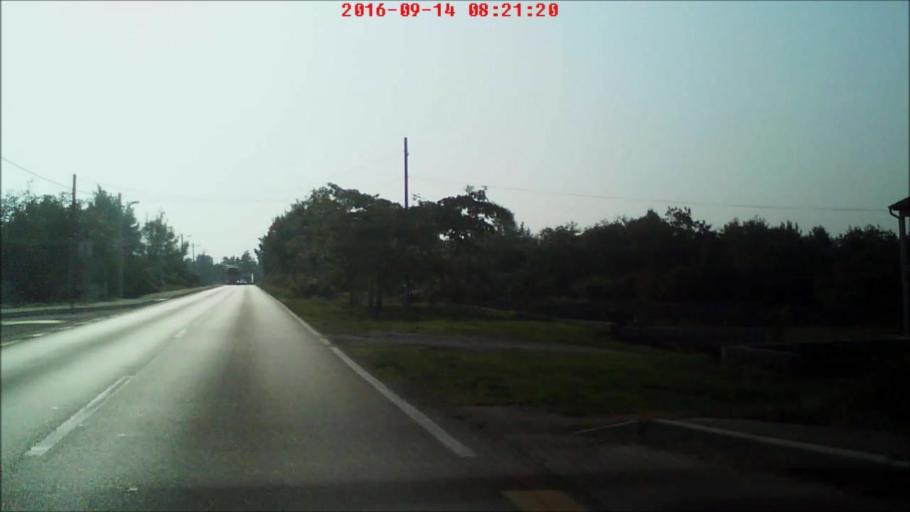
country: HR
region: Zadarska
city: Nin
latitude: 44.2226
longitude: 15.2102
